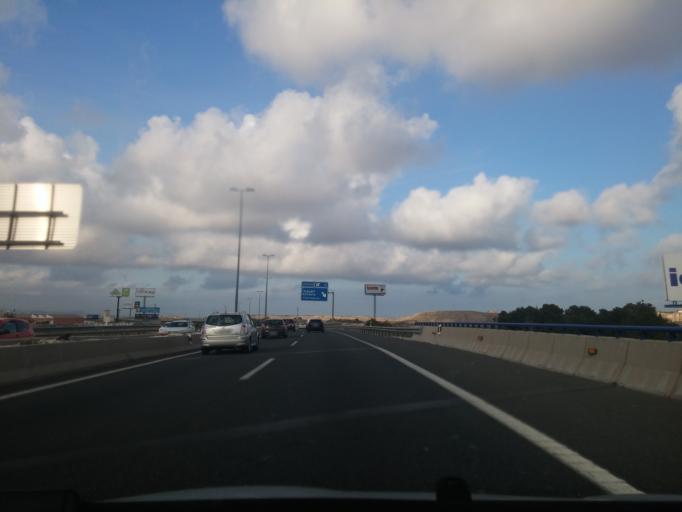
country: ES
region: Valencia
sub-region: Provincia de Alicante
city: San Vicent del Raspeig
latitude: 38.3796
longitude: -0.5014
